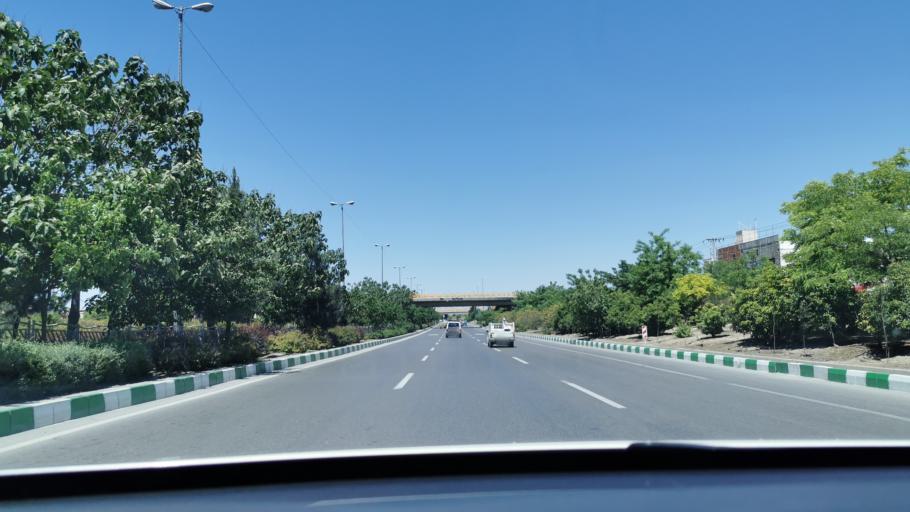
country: IR
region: Razavi Khorasan
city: Mashhad
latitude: 36.2655
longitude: 59.6535
